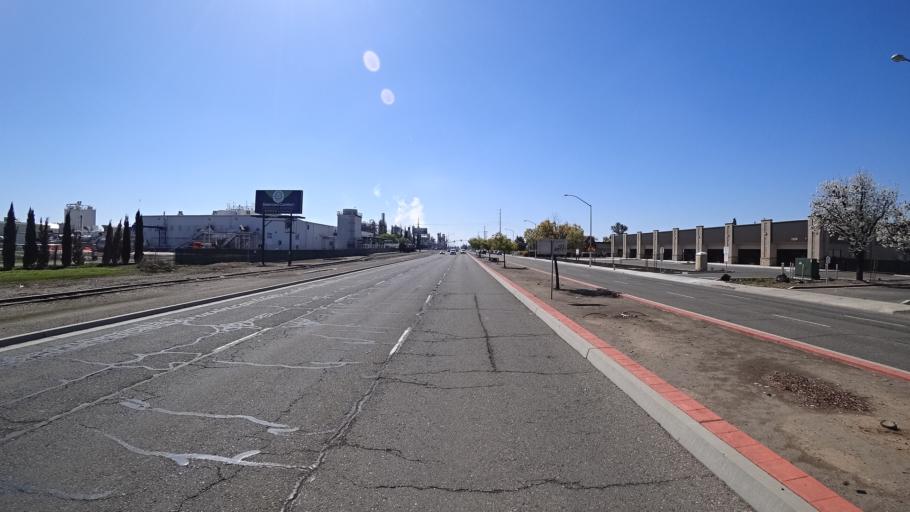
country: US
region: California
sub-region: Fresno County
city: Sunnyside
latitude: 36.7596
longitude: -119.7005
